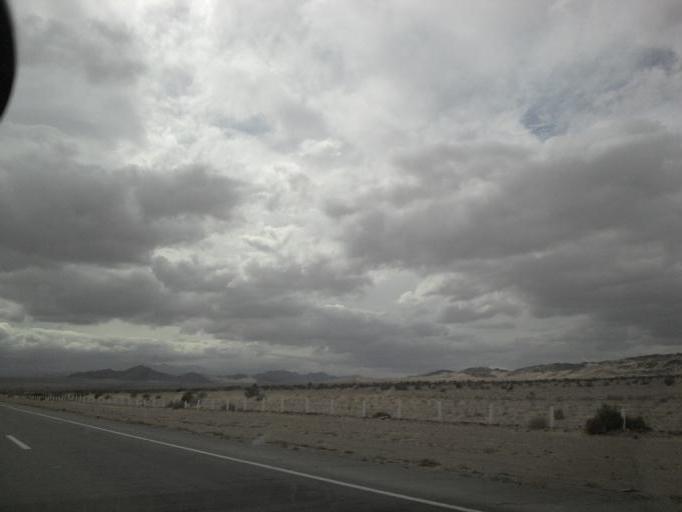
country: MX
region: Baja California
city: Progreso
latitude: 32.5756
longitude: -115.7538
